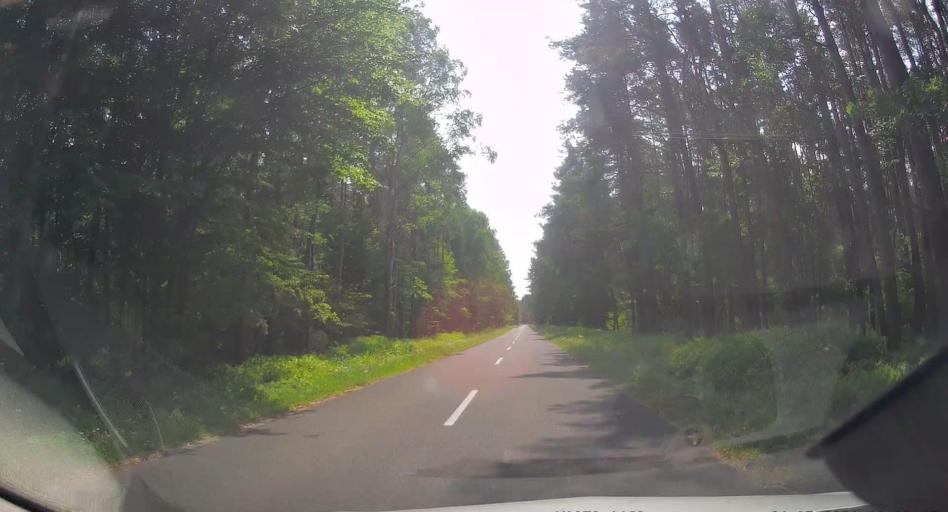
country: PL
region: Lodz Voivodeship
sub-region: Powiat tomaszowski
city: Lubochnia
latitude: 51.5594
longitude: 20.1291
